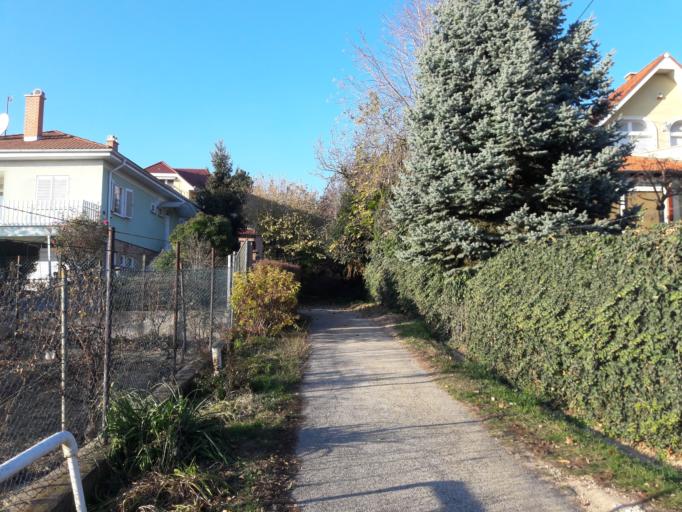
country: HU
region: Pest
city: Budaors
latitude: 47.4679
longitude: 18.9694
